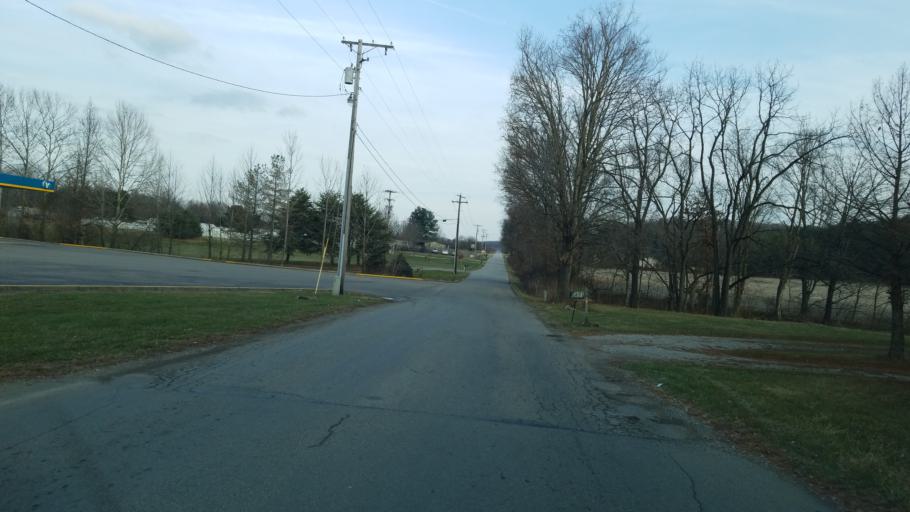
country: US
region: Ohio
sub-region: Ross County
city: Chillicothe
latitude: 39.2877
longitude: -82.8681
